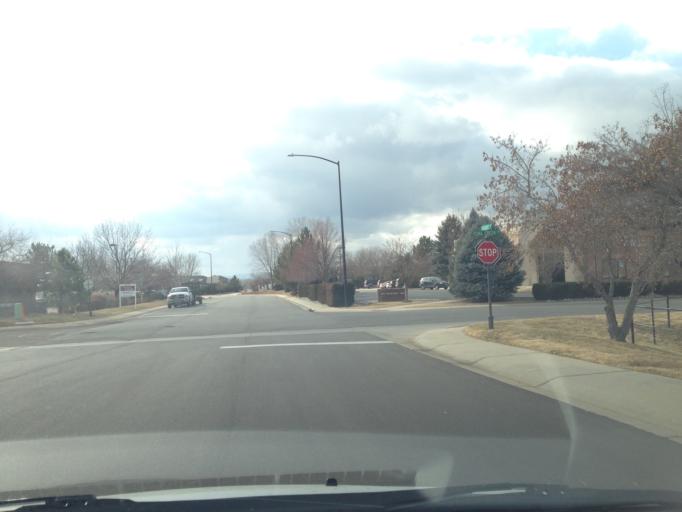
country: US
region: Colorado
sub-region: Boulder County
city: Lafayette
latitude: 39.9846
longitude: -105.0948
